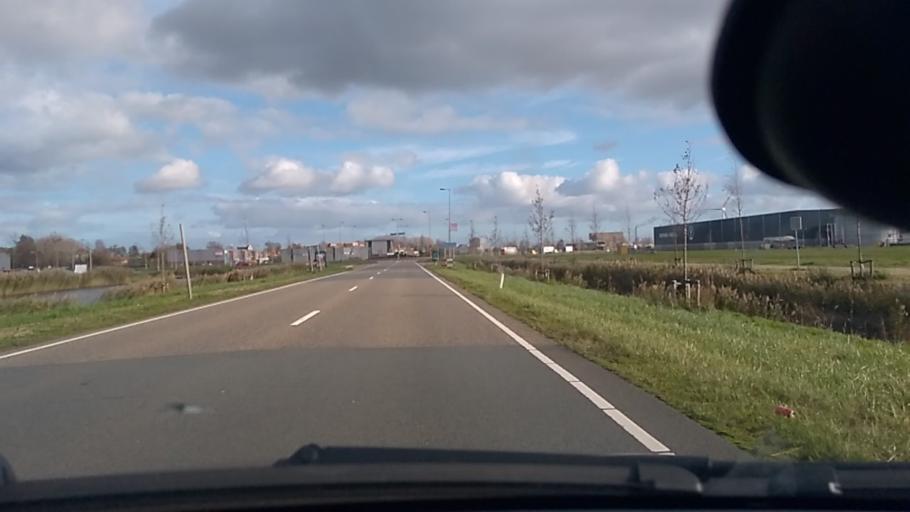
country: NL
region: North Holland
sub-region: Gemeente Zaanstad
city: Zaanstad
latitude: 52.4317
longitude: 4.7715
